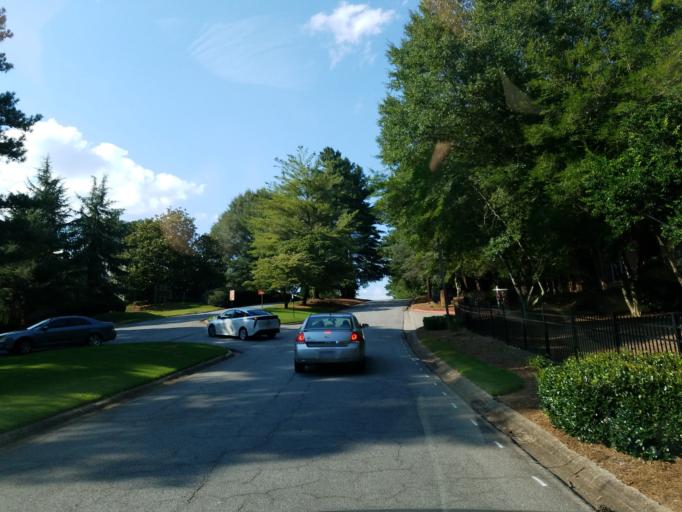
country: US
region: Georgia
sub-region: Fulton County
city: Roswell
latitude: 34.0050
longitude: -84.3383
